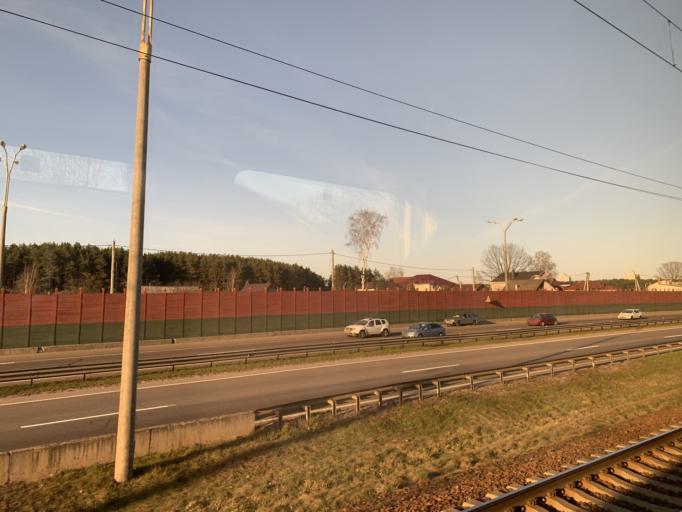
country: BY
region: Minsk
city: Zhdanovichy
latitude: 53.9518
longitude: 27.4112
